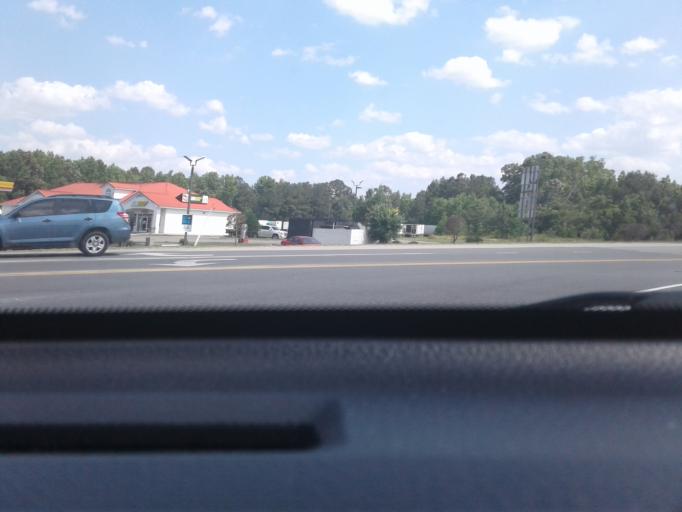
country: US
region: North Carolina
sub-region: Cumberland County
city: Eastover
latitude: 35.1225
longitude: -78.7509
